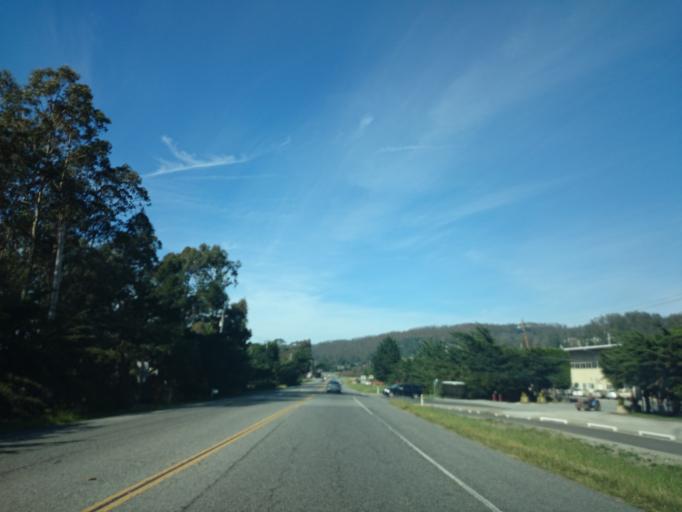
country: US
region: California
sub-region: San Mateo County
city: El Granada
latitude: 37.4876
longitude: -122.4492
